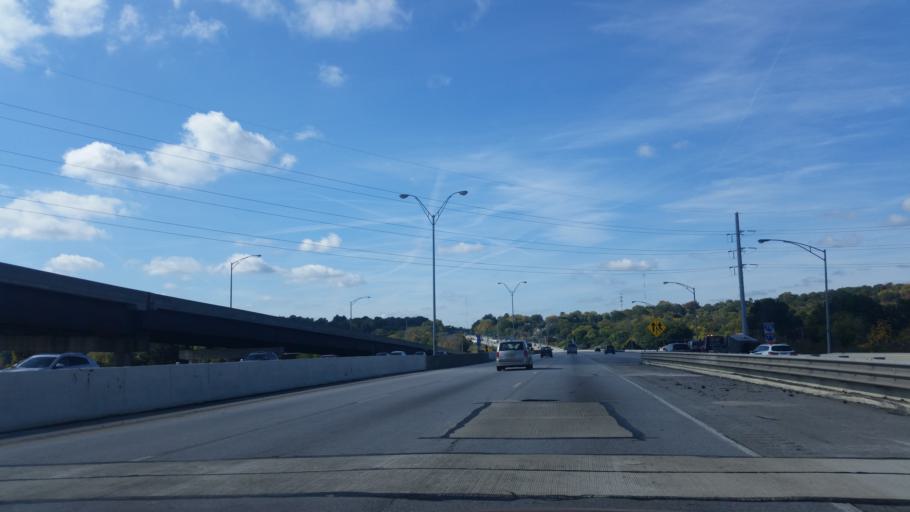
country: US
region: Ohio
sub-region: Summit County
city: Akron
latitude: 41.0621
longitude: -81.5399
